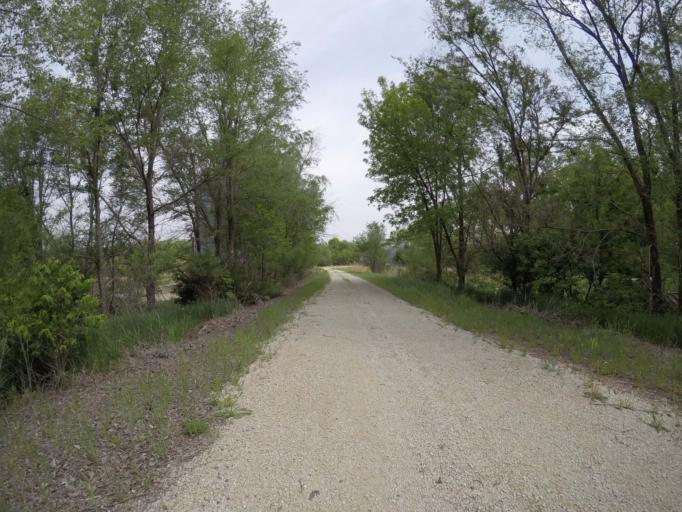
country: US
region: Nebraska
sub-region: Gage County
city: Wymore
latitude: 40.1998
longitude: -96.6608
